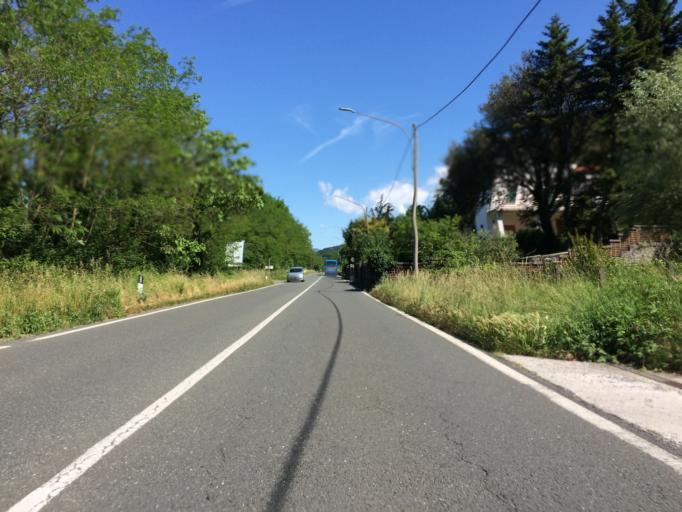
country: IT
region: Tuscany
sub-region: Provincia di Massa-Carrara
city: Terrarossa
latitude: 44.2342
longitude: 9.9604
